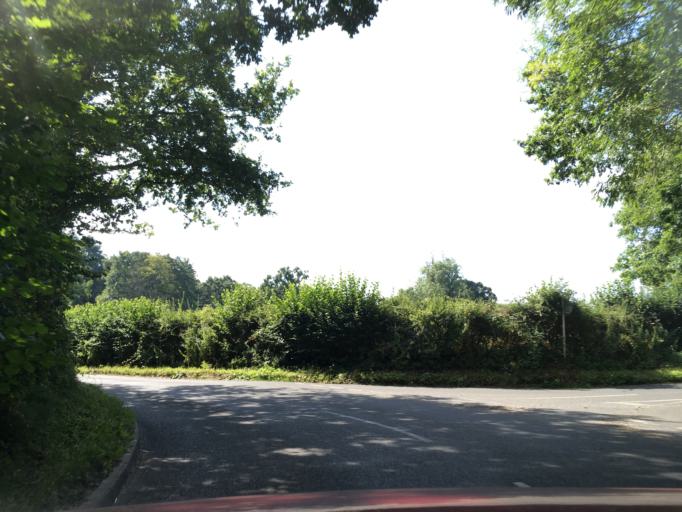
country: GB
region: England
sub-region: Hampshire
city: Highclere
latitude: 51.3670
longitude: -1.4044
